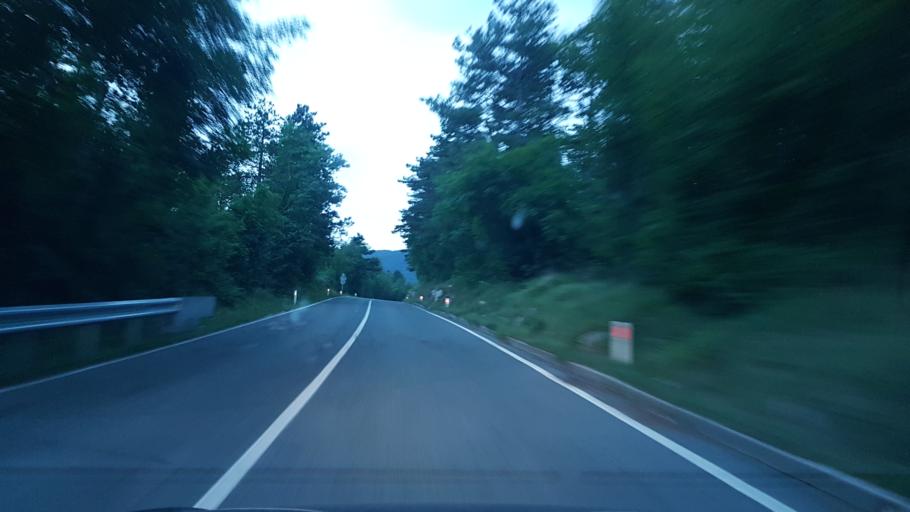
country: SI
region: Divaca
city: Divaca
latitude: 45.6641
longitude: 13.9406
